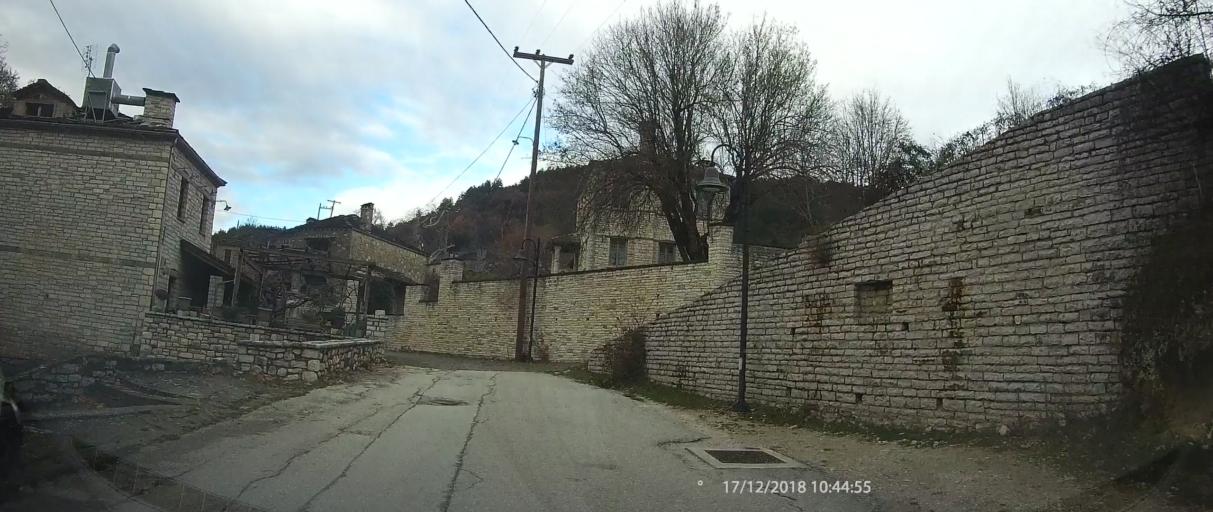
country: GR
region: Epirus
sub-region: Nomos Ioanninon
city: Konitsa
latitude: 39.9680
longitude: 20.7199
